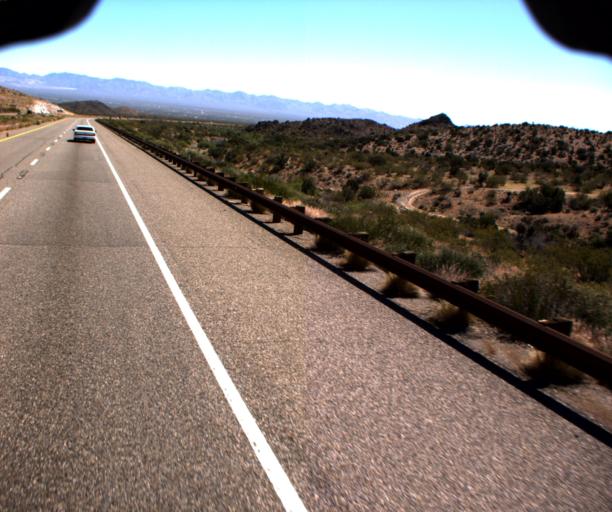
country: US
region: Arizona
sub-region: Mohave County
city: Golden Valley
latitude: 35.2259
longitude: -114.3798
